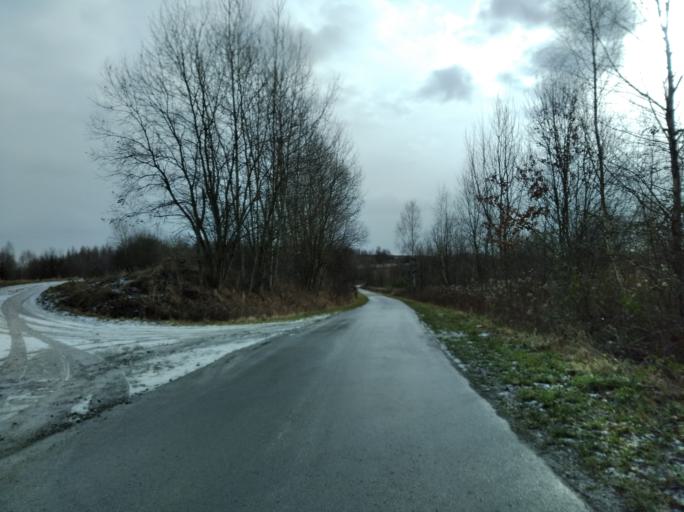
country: PL
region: Subcarpathian Voivodeship
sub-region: Powiat strzyzowski
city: Wysoka Strzyzowska
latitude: 49.8911
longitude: 21.7275
